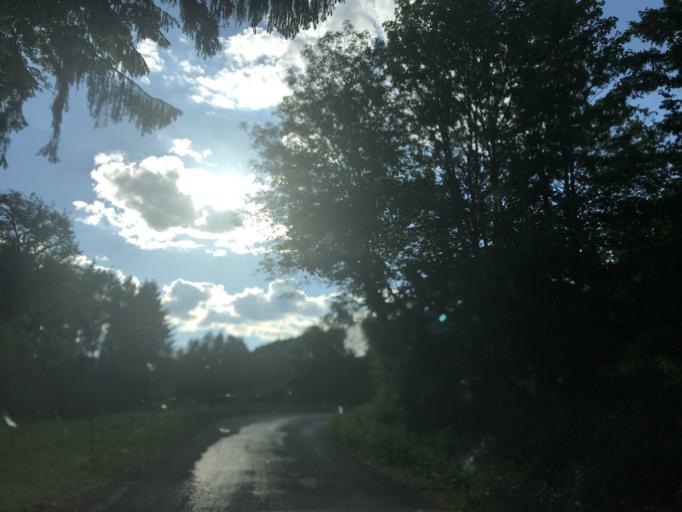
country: FR
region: Auvergne
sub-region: Departement du Puy-de-Dome
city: Job
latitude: 45.7119
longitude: 3.6985
